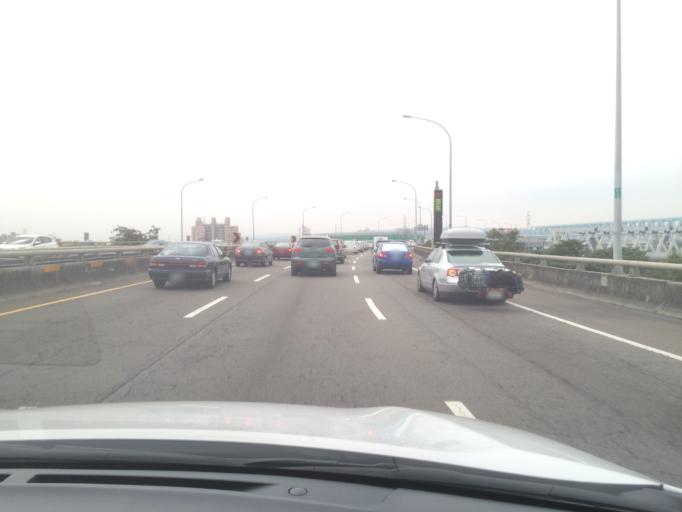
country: TW
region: Taiwan
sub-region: Changhua
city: Chang-hua
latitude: 24.1127
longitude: 120.6204
